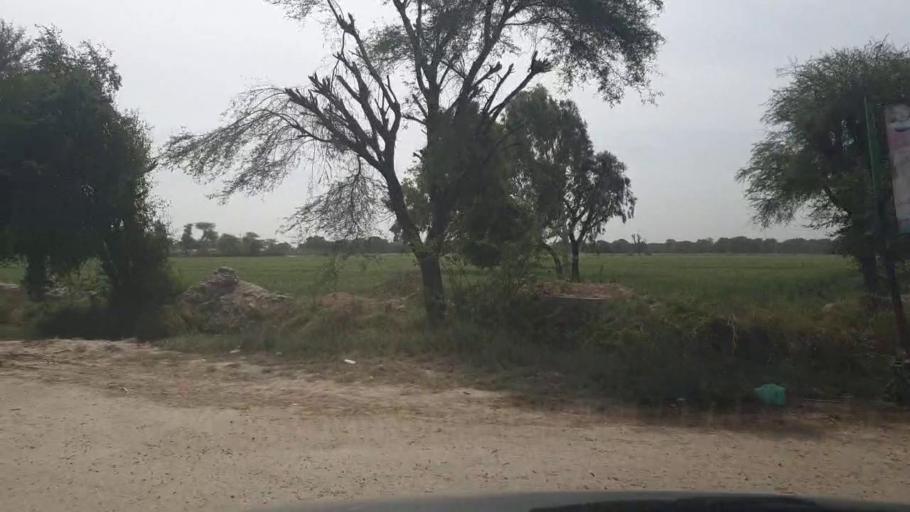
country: PK
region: Sindh
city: Umarkot
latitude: 25.2331
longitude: 69.6968
